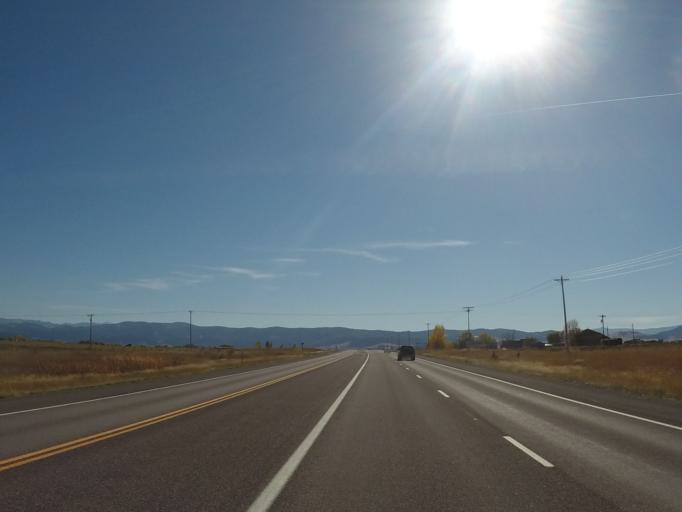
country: US
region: Montana
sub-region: Lake County
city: Ronan
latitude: 47.3722
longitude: -114.0971
